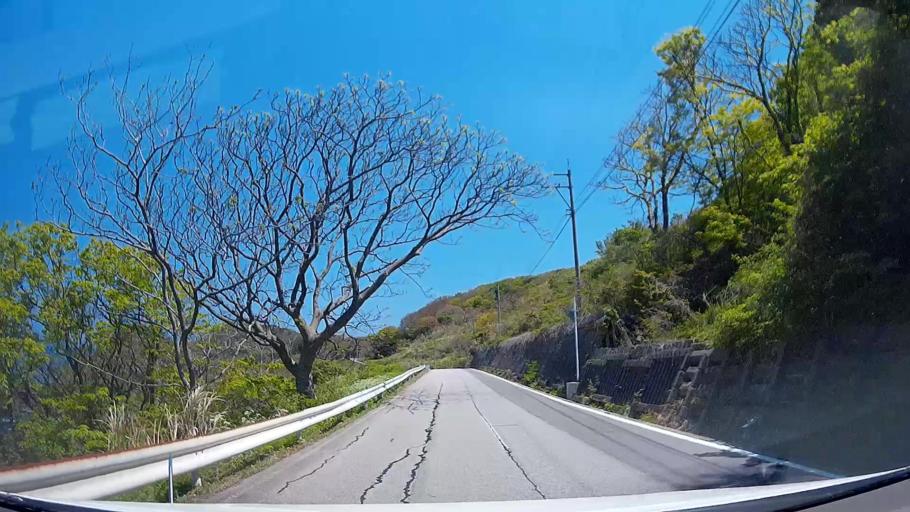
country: JP
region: Ishikawa
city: Nanao
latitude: 37.5282
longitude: 137.2699
